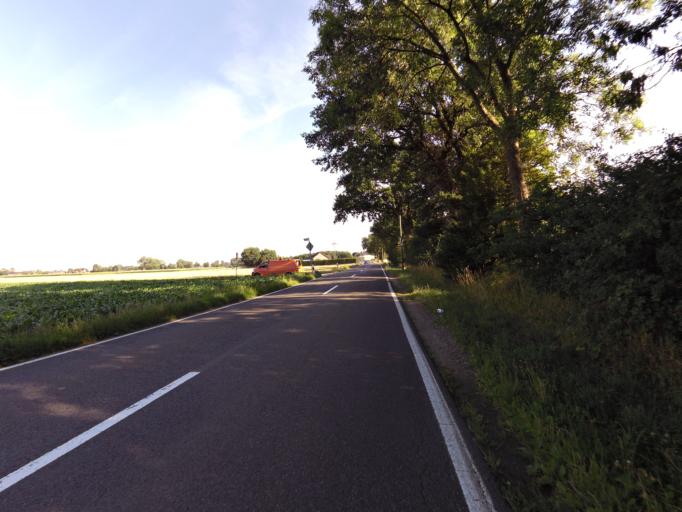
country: DE
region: North Rhine-Westphalia
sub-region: Regierungsbezirk Koln
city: Wassenberg
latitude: 51.0504
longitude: 6.1737
